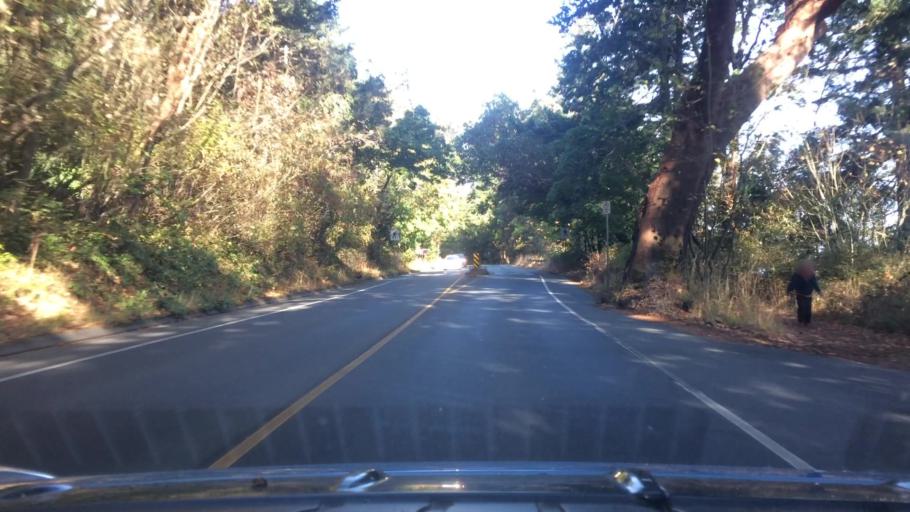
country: CA
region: British Columbia
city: Oak Bay
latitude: 48.4990
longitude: -123.3392
